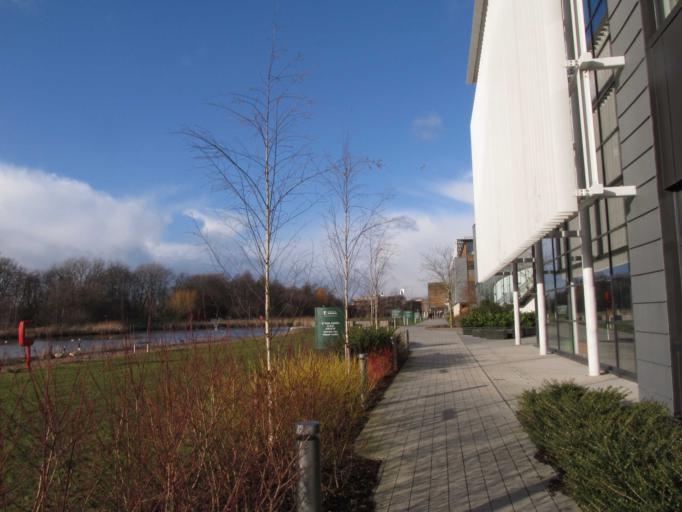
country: GB
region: England
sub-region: Nottingham
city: Nottingham
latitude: 52.9507
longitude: -1.1863
